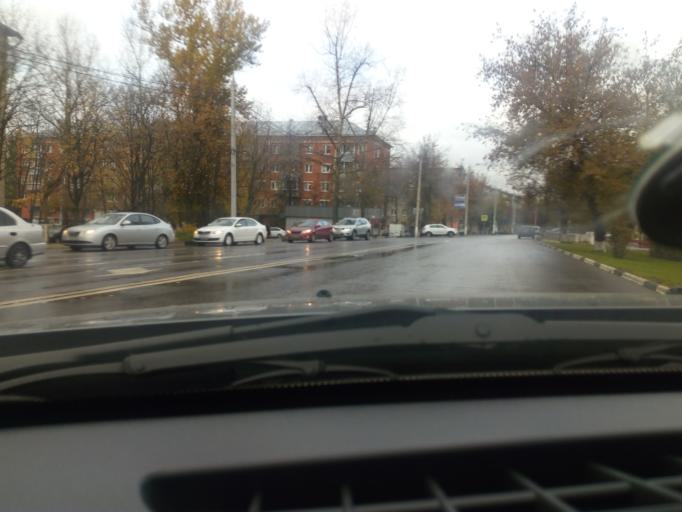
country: RU
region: Moskovskaya
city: Domodedovo
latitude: 55.4404
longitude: 37.7660
